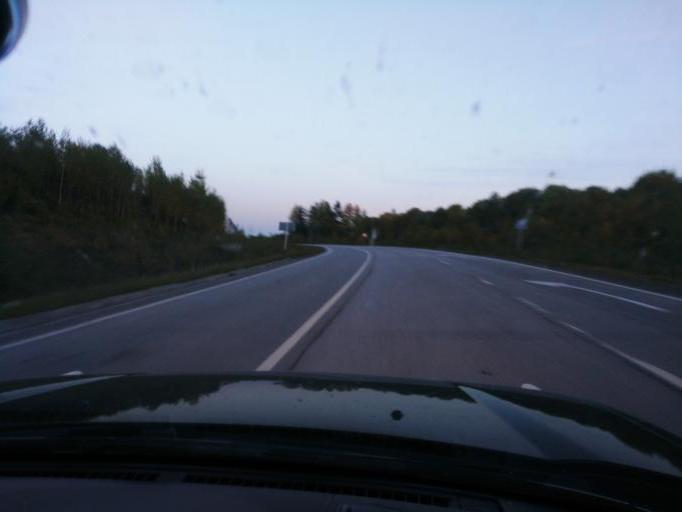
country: RU
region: Perm
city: Verkhnechusovskiye Gorodki
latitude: 58.2847
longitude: 56.8982
